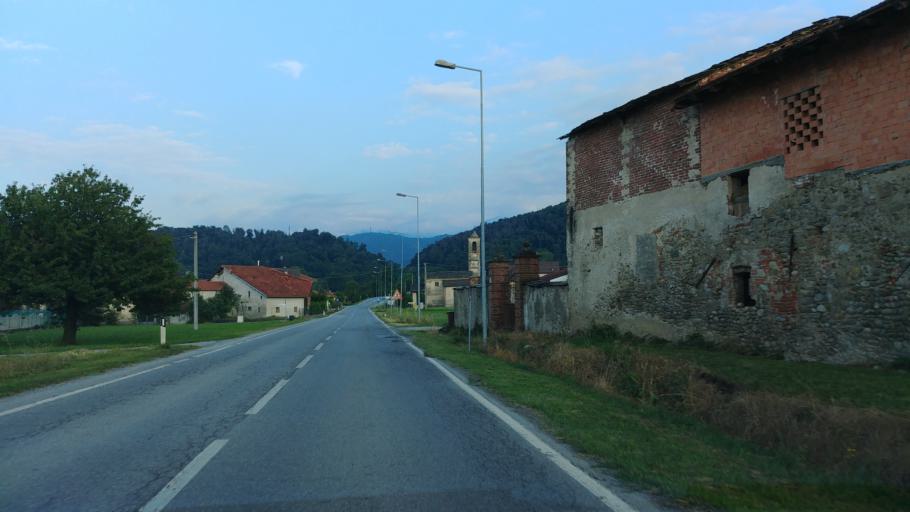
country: IT
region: Piedmont
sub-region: Provincia di Cuneo
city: Peveragno
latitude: 44.3388
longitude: 7.6020
